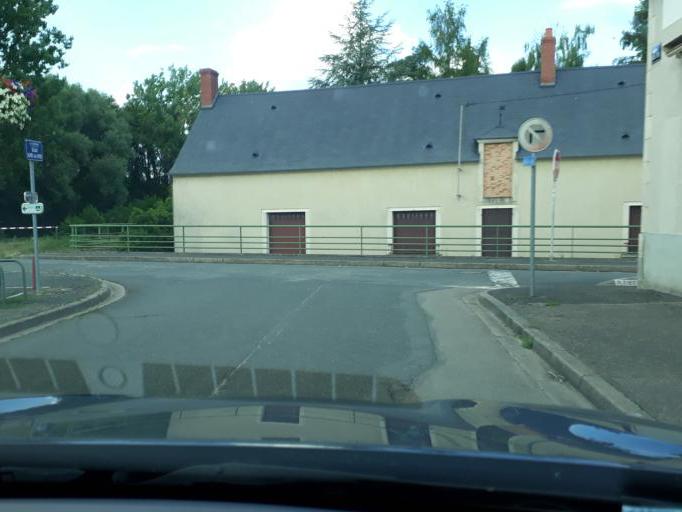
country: FR
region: Centre
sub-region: Departement du Cher
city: Jouet-sur-l'Aubois
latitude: 46.9518
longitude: 2.9451
